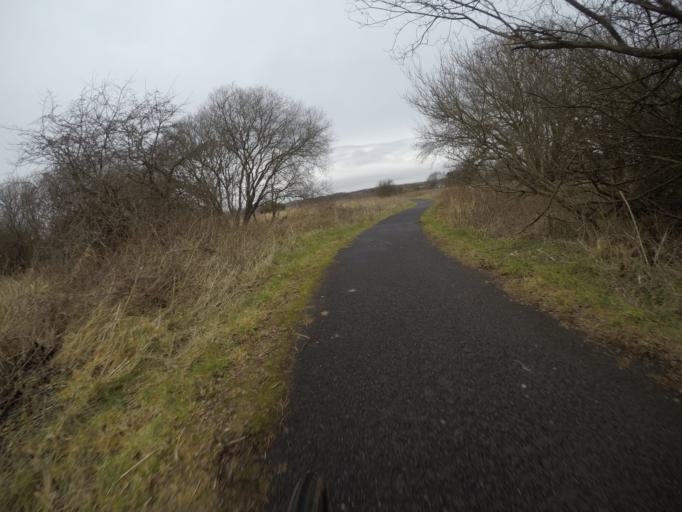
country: GB
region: Scotland
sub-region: North Ayrshire
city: Kilwinning
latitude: 55.6327
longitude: -4.6912
